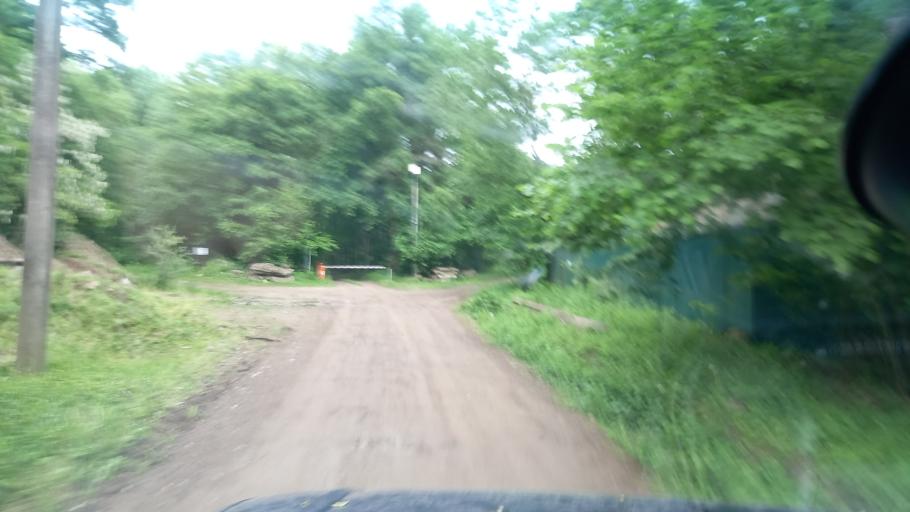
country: RU
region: Krasnodarskiy
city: Azovskaya
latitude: 44.6343
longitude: 38.6215
